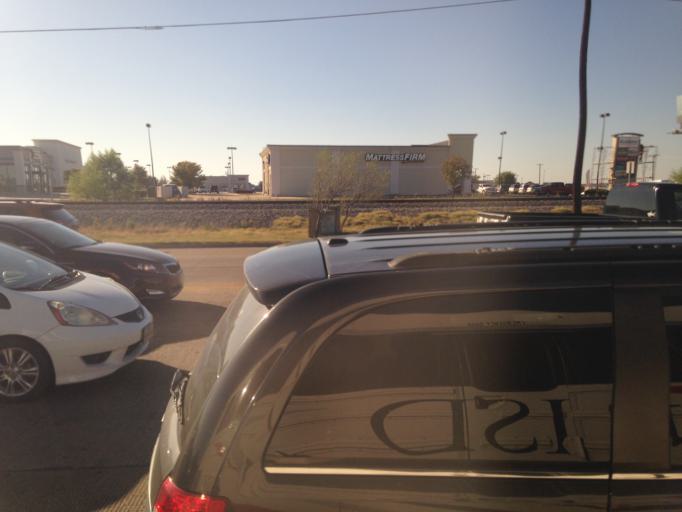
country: US
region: Texas
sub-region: Tarrant County
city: Watauga
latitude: 32.8939
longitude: -97.2587
